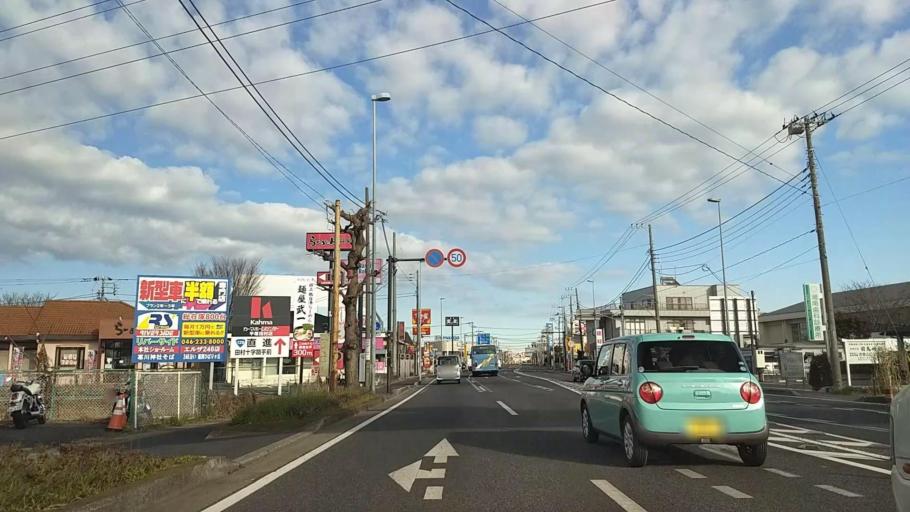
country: JP
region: Kanagawa
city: Hiratsuka
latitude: 35.3532
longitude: 139.3564
